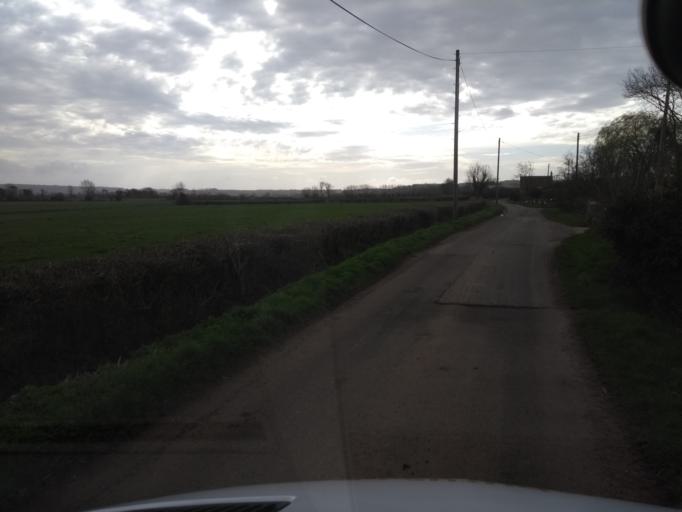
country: GB
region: England
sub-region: Somerset
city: Langport
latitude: 51.0881
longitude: -2.8048
